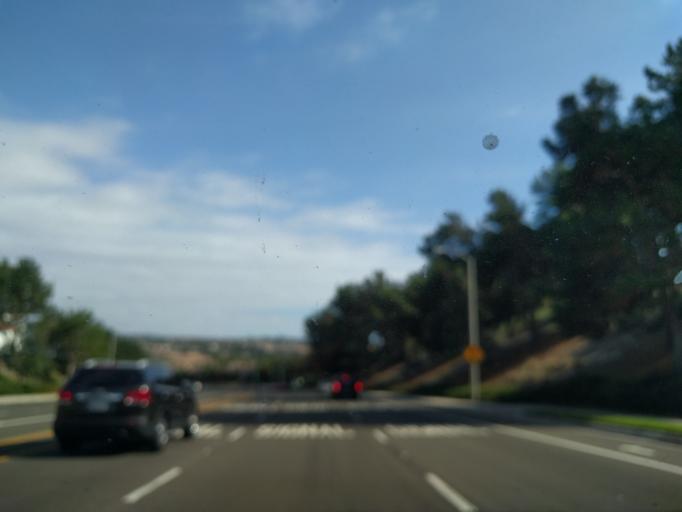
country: US
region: California
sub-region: Orange County
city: Aliso Viejo
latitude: 33.5588
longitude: -117.7251
